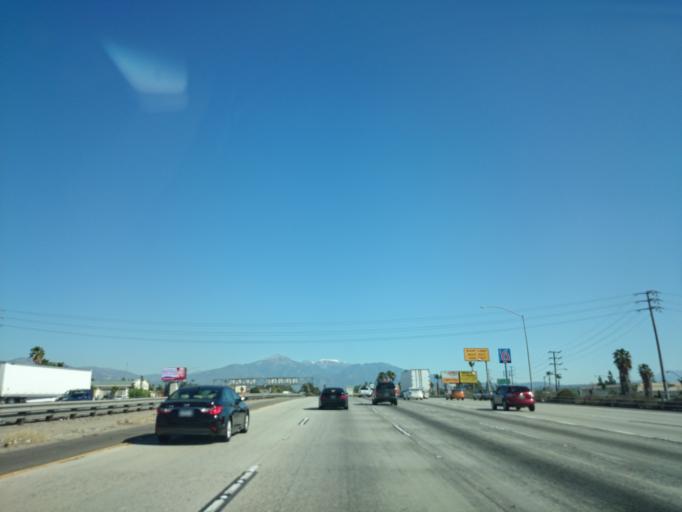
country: US
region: California
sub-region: San Bernardino County
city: Colton
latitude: 34.0635
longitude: -117.2889
